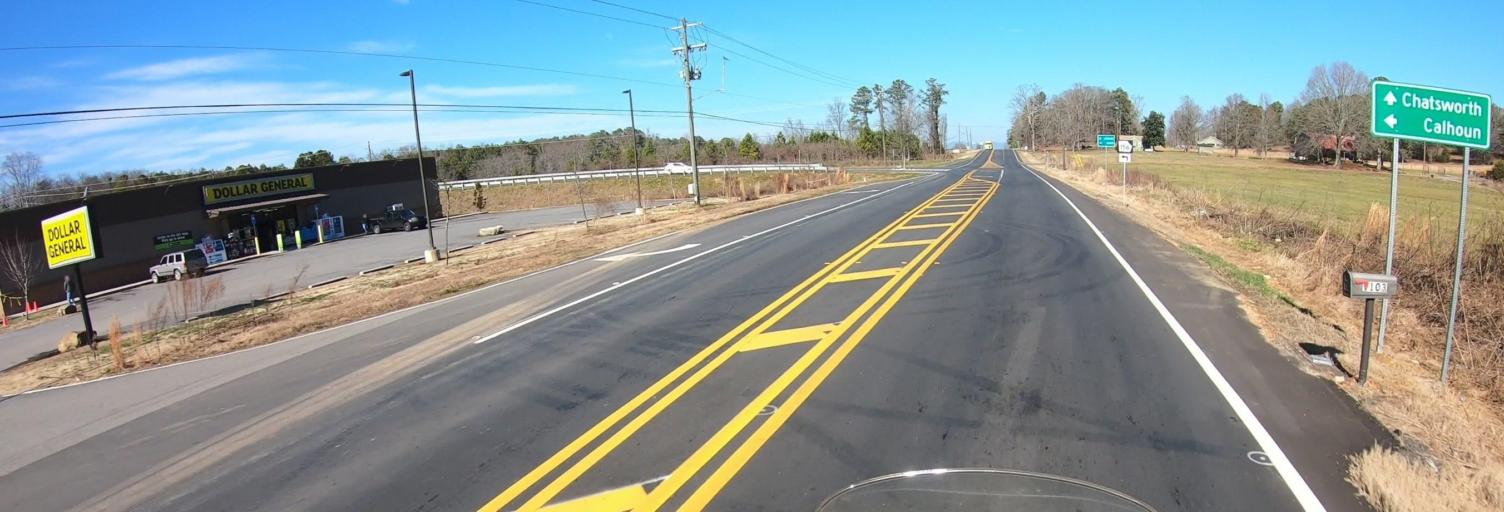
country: US
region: Georgia
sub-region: Bartow County
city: Rydal
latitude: 34.5285
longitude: -84.7066
